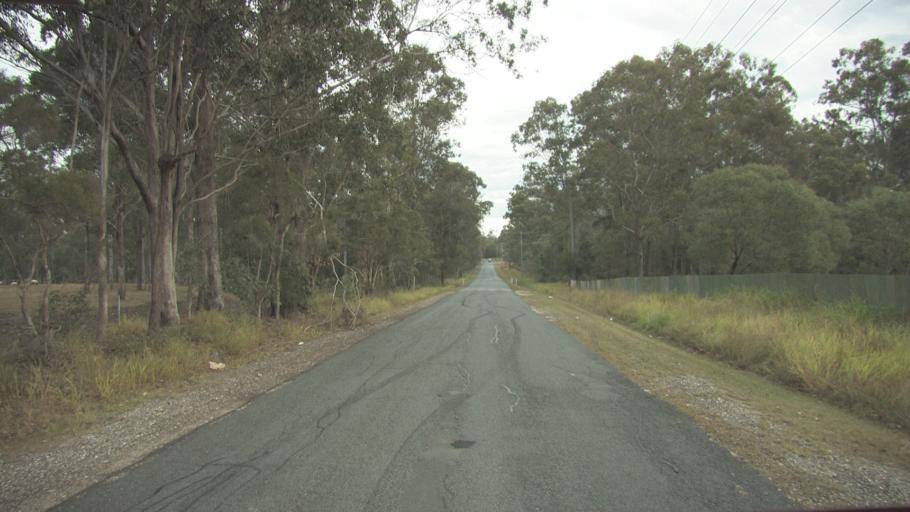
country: AU
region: Queensland
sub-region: Logan
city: Chambers Flat
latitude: -27.7719
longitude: 153.1159
